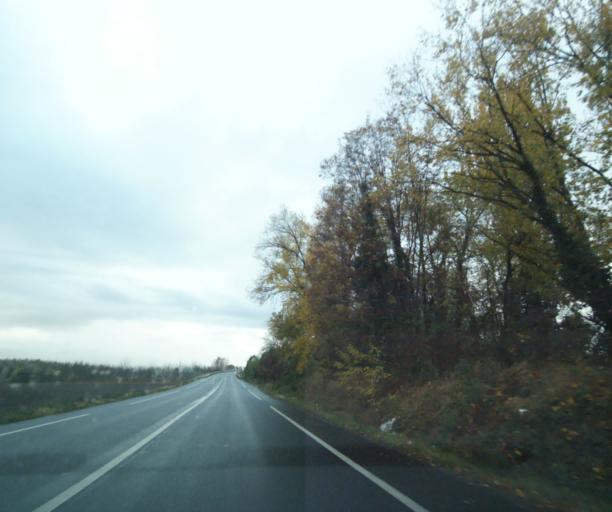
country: FR
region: Auvergne
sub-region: Departement du Puy-de-Dome
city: Aulnat
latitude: 45.7750
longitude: 3.1472
